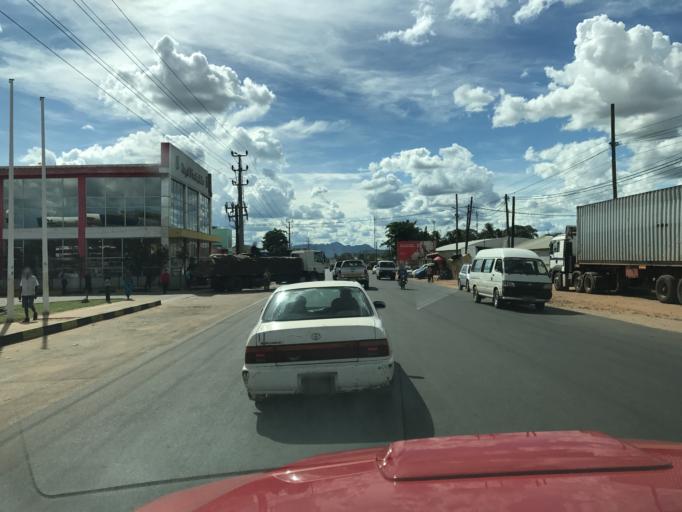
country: MZ
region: Nampula
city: Nampula
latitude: -15.1100
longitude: 39.2502
